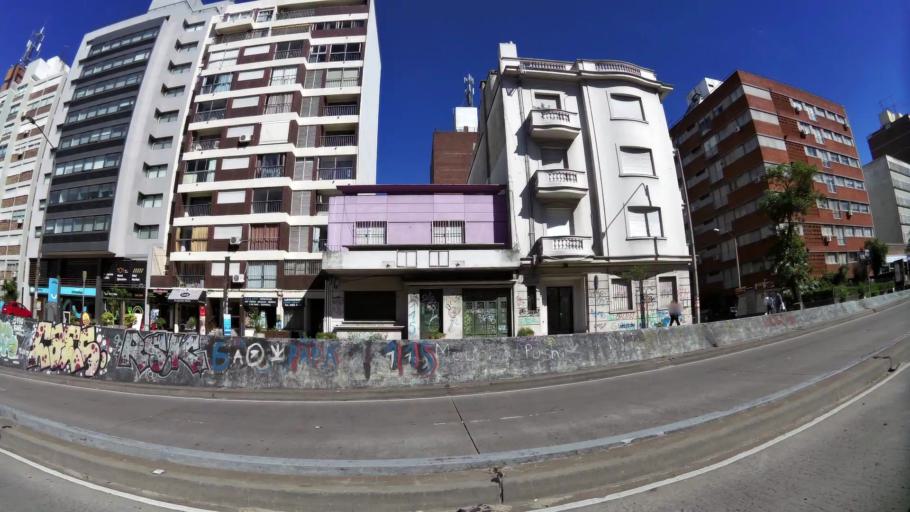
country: UY
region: Montevideo
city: Montevideo
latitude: -34.8931
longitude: -56.1631
